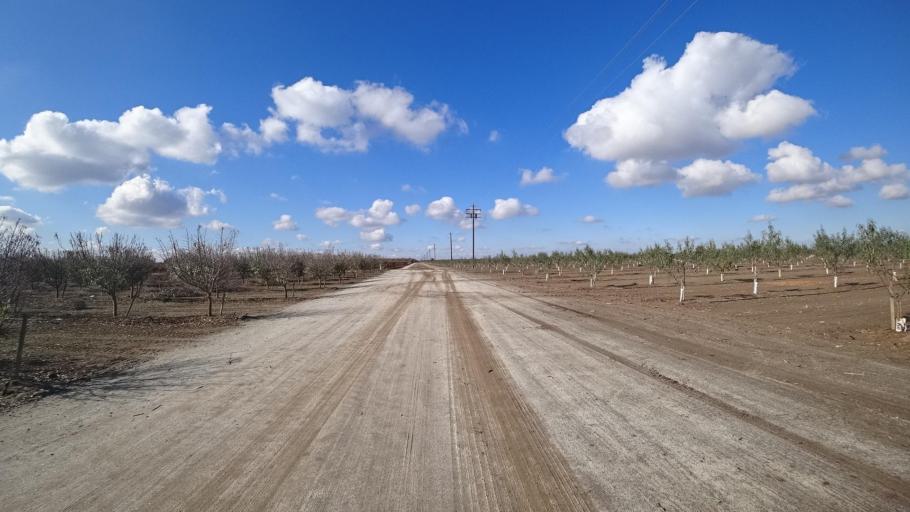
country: US
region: California
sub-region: Kern County
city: McFarland
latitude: 35.6527
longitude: -119.2267
